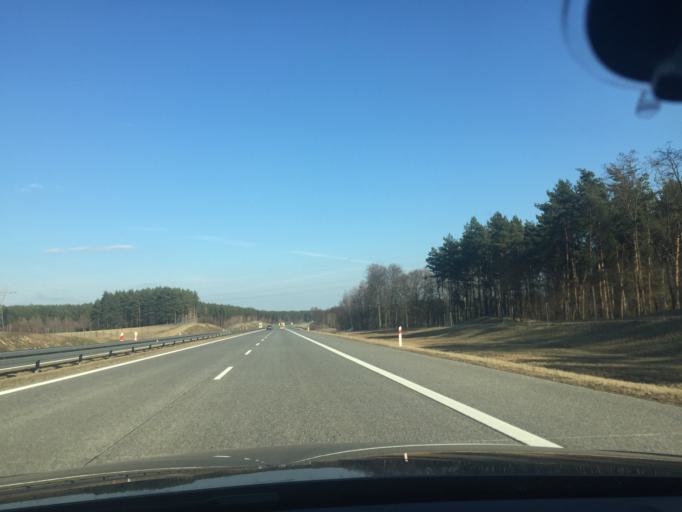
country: PL
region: Lubusz
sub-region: Powiat swiebodzinski
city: Sieniawa
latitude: 52.3144
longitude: 15.3720
